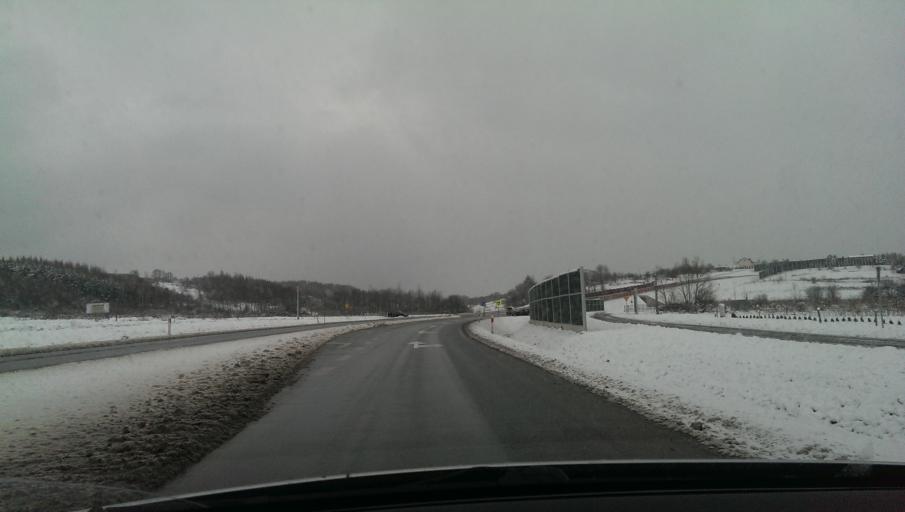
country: PL
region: Subcarpathian Voivodeship
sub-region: Powiat brzozowski
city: Brzozow
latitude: 49.7020
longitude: 22.0344
